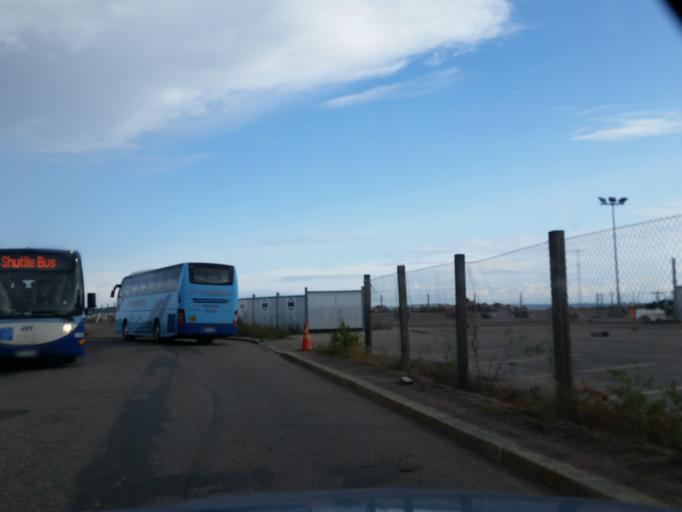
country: FI
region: Uusimaa
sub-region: Helsinki
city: Helsinki
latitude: 60.1483
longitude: 24.9251
